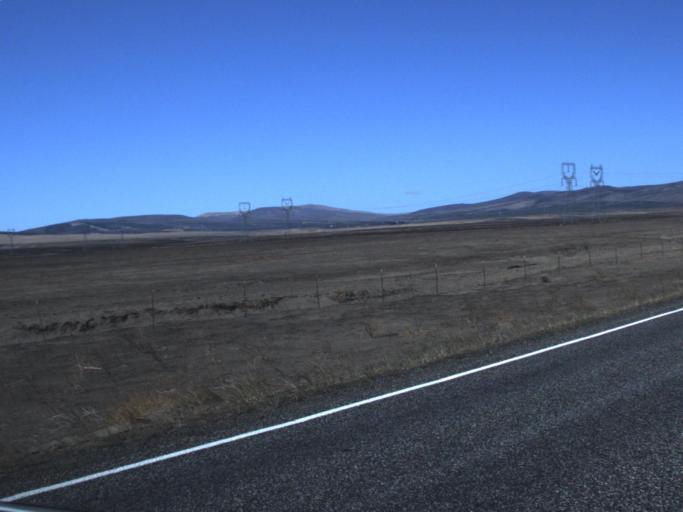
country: US
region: Washington
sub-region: Grant County
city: Desert Aire
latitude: 46.5573
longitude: -119.7041
